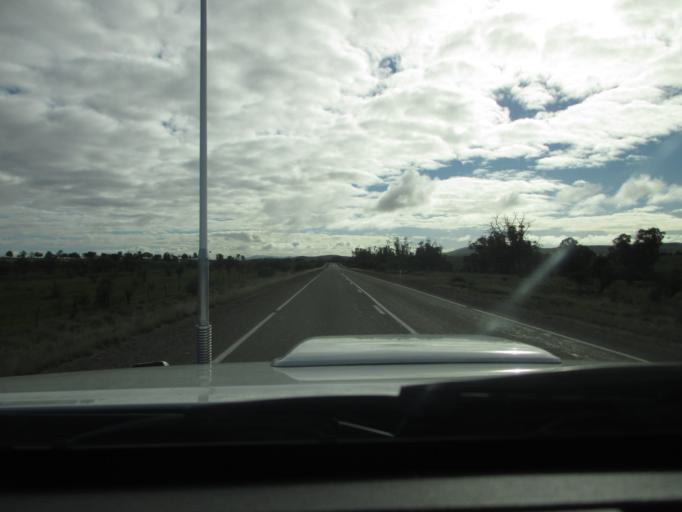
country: AU
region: South Australia
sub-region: Flinders Ranges
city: Quorn
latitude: -32.5060
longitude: 138.5468
